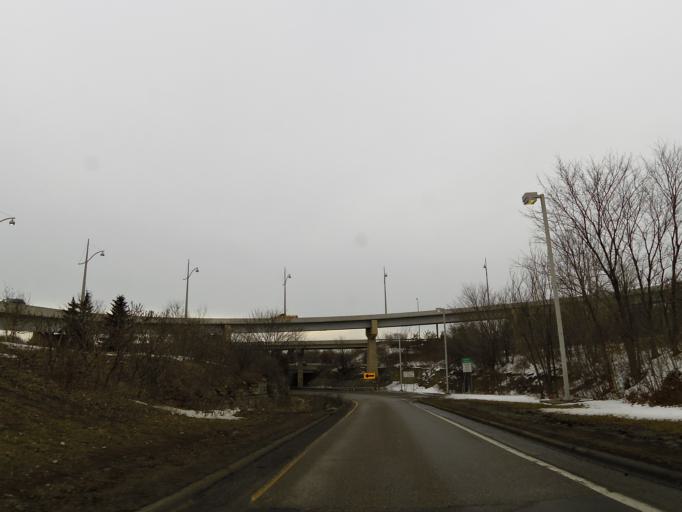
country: US
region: Minnesota
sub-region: Dakota County
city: Mendota Heights
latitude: 44.8781
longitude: -93.1960
